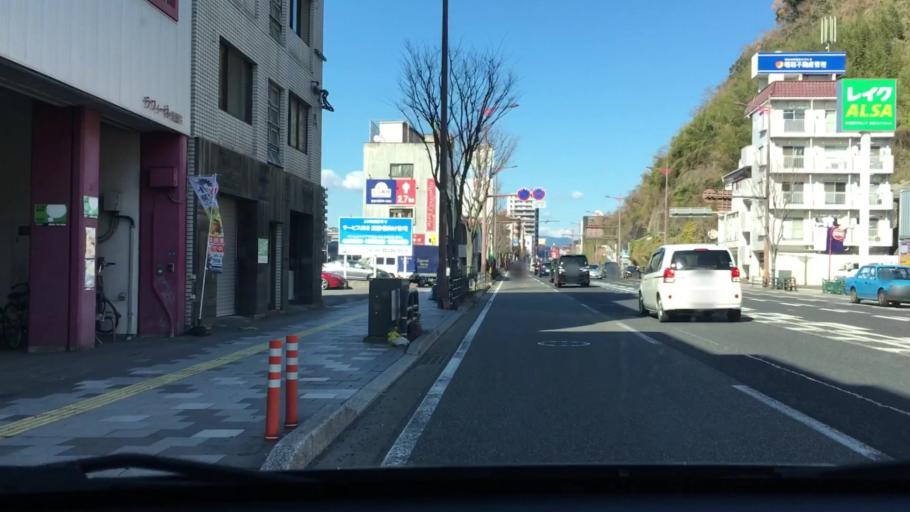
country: JP
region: Kagoshima
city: Kagoshima-shi
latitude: 31.5955
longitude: 130.5423
